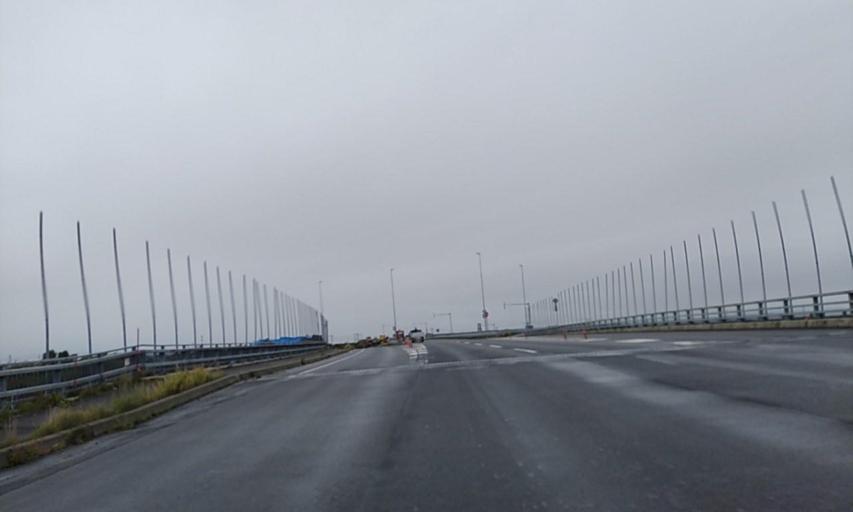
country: JP
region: Hokkaido
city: Kushiro
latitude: 43.0357
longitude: 144.3178
